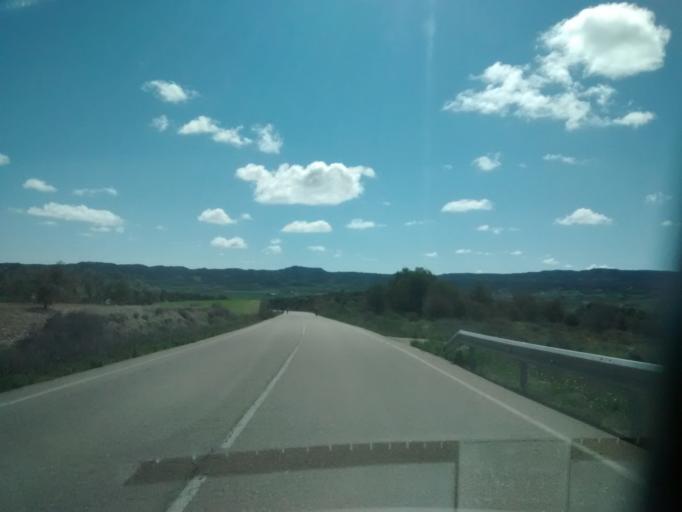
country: ES
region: Aragon
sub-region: Provincia de Zaragoza
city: Lecinena
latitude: 41.7905
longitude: -0.6312
